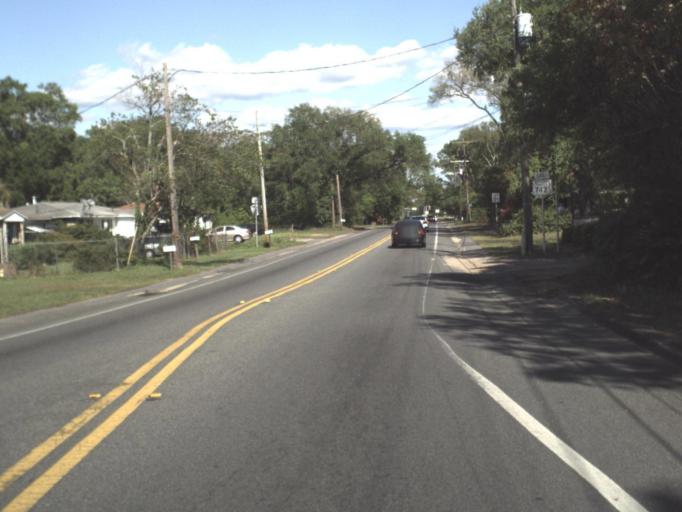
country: US
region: Florida
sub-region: Escambia County
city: Ensley
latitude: 30.4972
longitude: -87.2545
